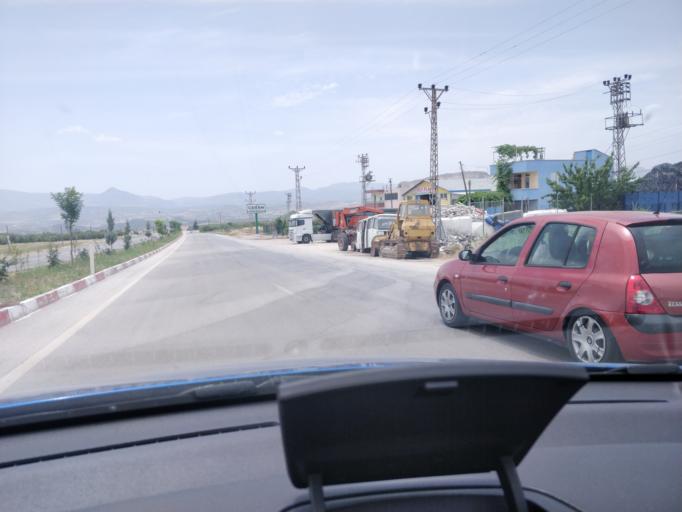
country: TR
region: Mersin
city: Mut
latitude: 36.6075
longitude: 33.4378
